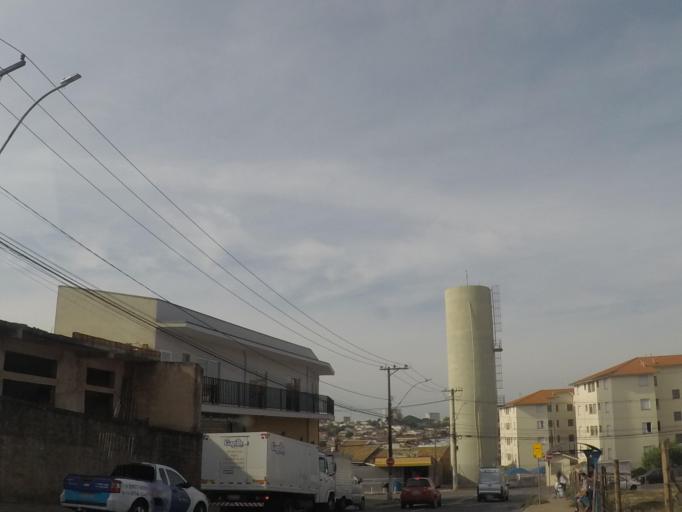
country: BR
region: Sao Paulo
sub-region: Hortolandia
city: Hortolandia
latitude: -22.8640
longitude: -47.2022
